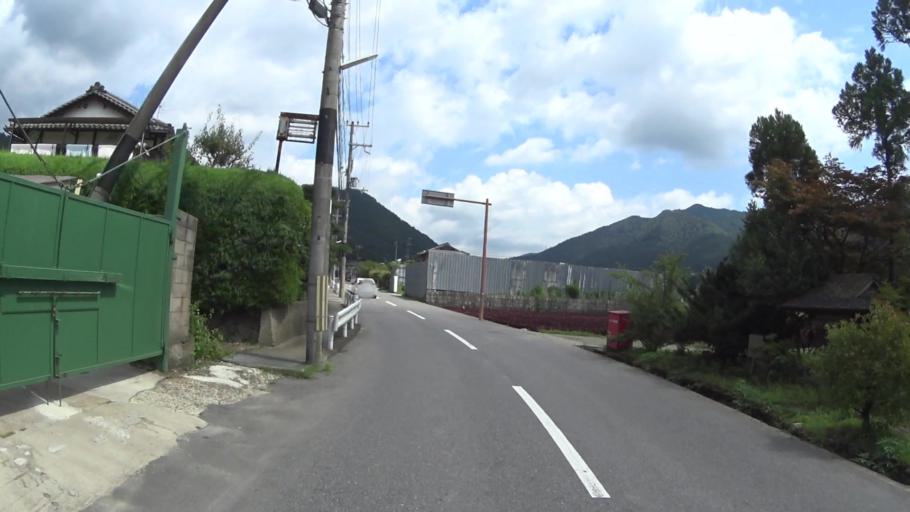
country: JP
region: Kyoto
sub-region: Kyoto-shi
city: Kamigyo-ku
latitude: 35.1121
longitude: 135.8220
